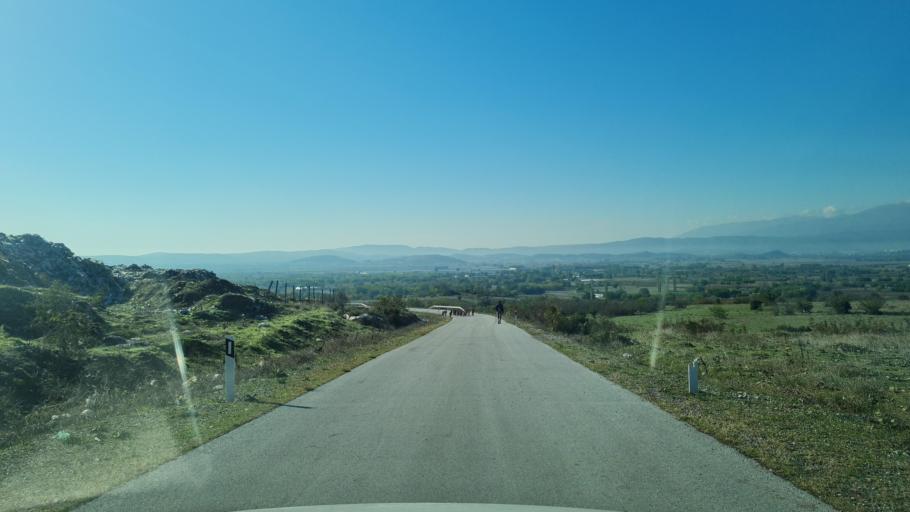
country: MK
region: Bogdanci
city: Bogdanci
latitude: 41.1995
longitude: 22.5618
